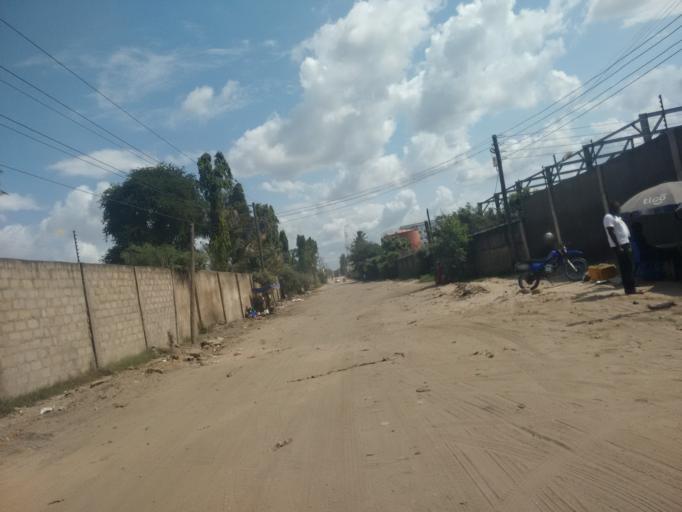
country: TZ
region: Dar es Salaam
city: Dar es Salaam
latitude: -6.8430
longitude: 39.2637
